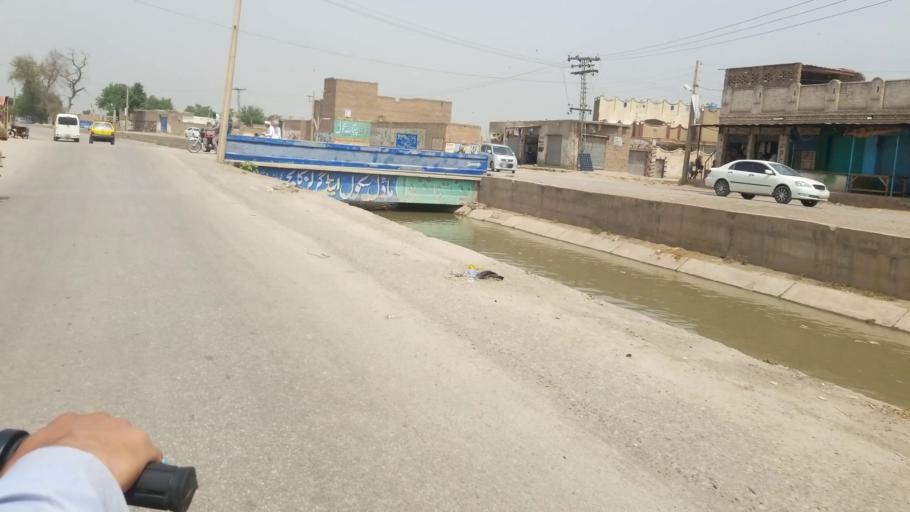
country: PK
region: Khyber Pakhtunkhwa
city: Peshawar
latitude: 33.9561
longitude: 71.5503
